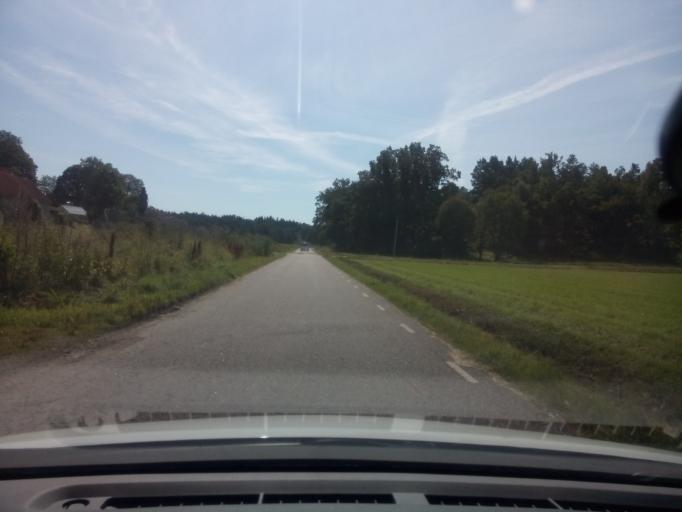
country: SE
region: Soedermanland
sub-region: Trosa Kommun
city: Trosa
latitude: 58.8086
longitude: 17.3621
